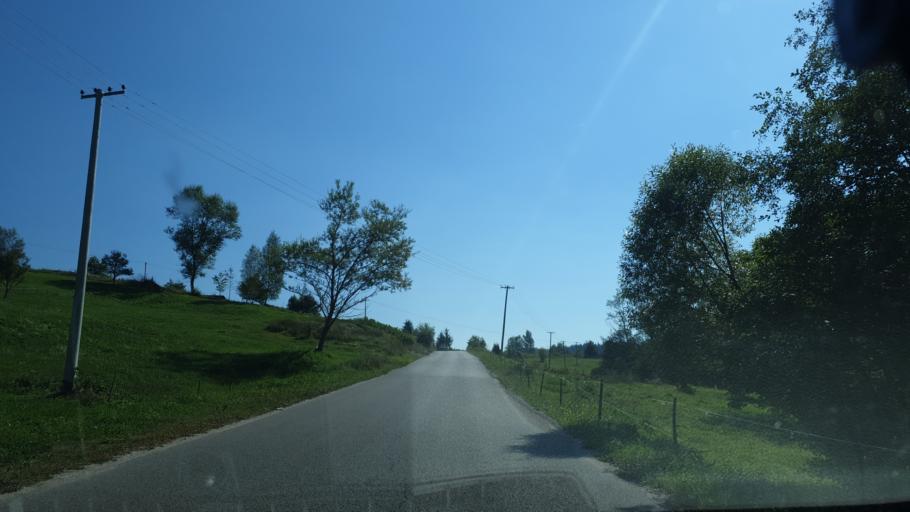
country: RS
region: Central Serbia
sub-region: Zlatiborski Okrug
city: Nova Varos
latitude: 43.4376
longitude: 19.8675
